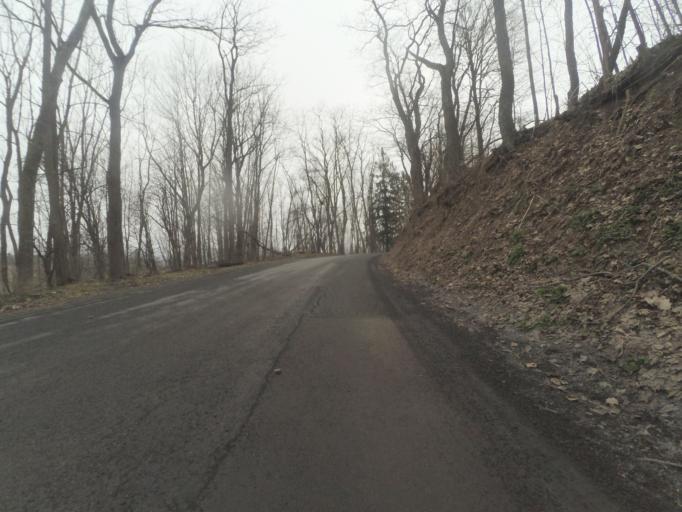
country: US
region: Pennsylvania
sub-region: Centre County
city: Centre Hall
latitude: 40.8127
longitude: -77.6272
